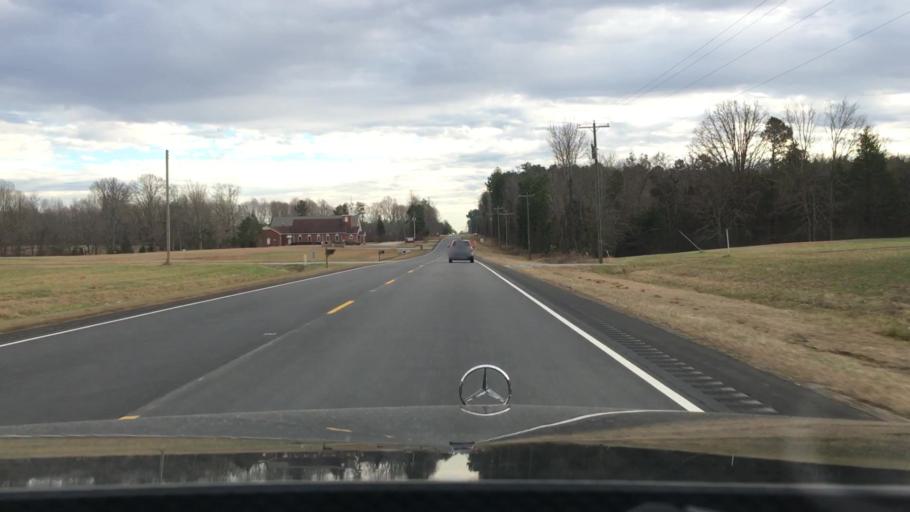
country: US
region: North Carolina
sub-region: Alamance County
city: Mebane
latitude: 36.2614
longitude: -79.1948
